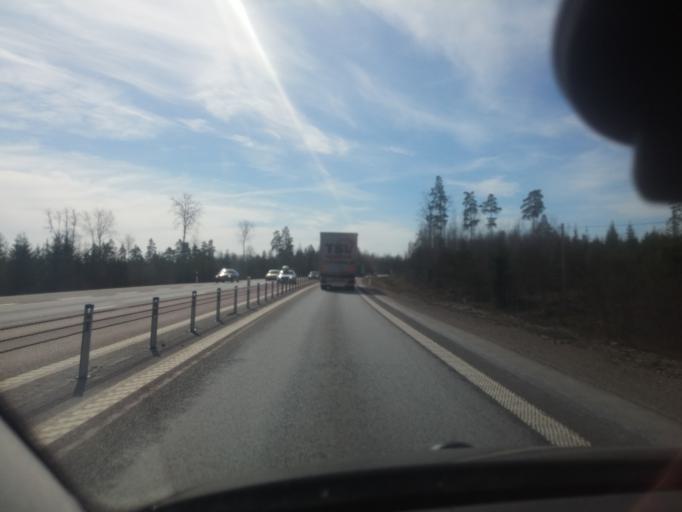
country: SE
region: Gaevleborg
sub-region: Gavle Kommun
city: Gavle
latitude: 60.7936
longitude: 17.0827
